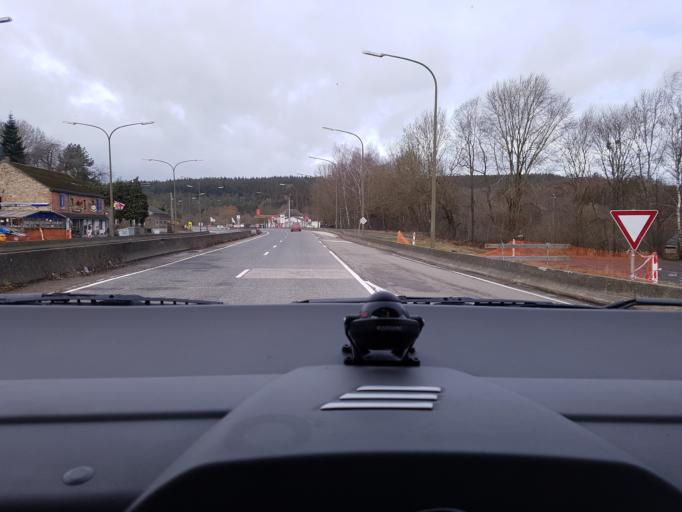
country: BE
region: Wallonia
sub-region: Province du Luxembourg
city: Nassogne
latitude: 50.1613
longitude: 5.4077
